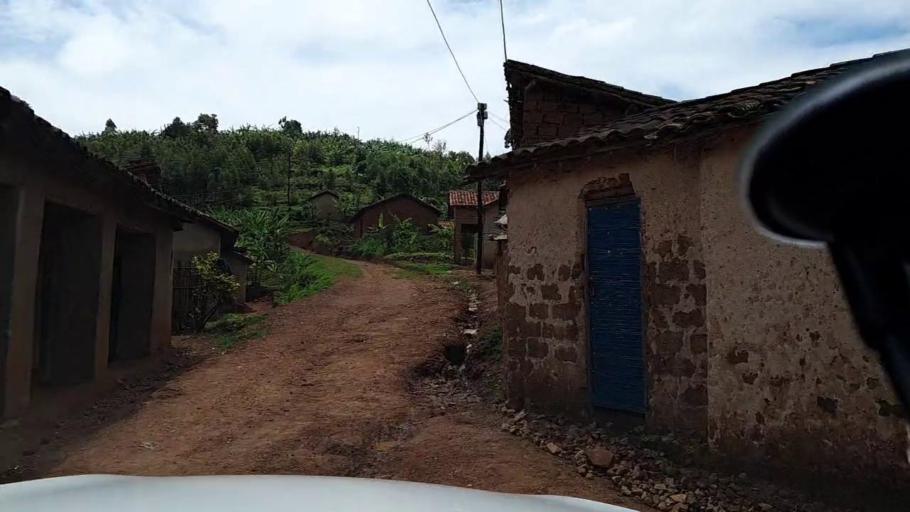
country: RW
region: Southern Province
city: Gitarama
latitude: -2.0752
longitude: 29.6693
